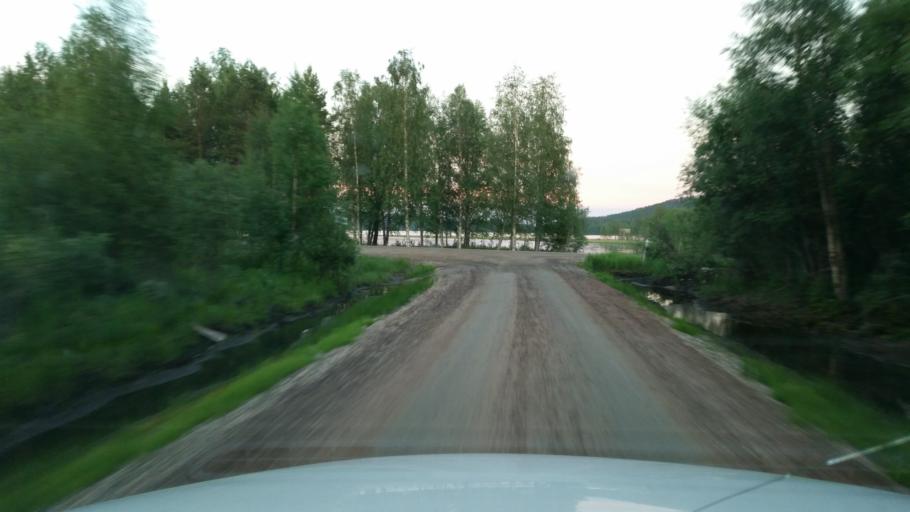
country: SE
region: Vaesternorrland
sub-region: Ange Kommun
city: Ange
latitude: 62.1838
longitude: 15.6372
